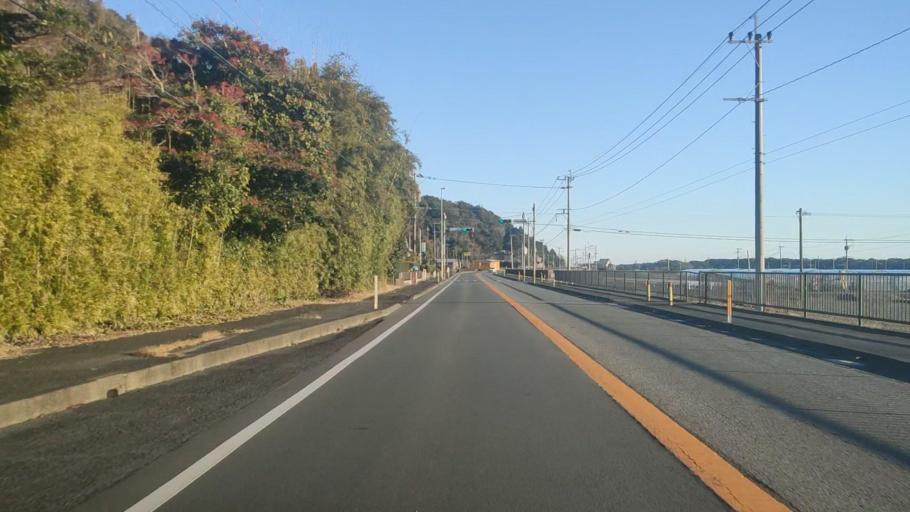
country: JP
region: Miyazaki
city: Takanabe
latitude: 32.0923
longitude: 131.5152
